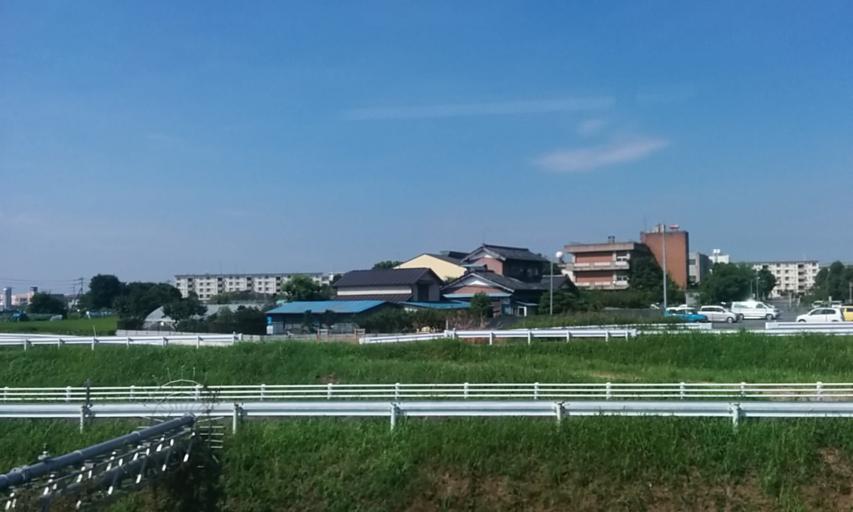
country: JP
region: Saitama
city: Kukichuo
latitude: 36.0899
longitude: 139.6645
